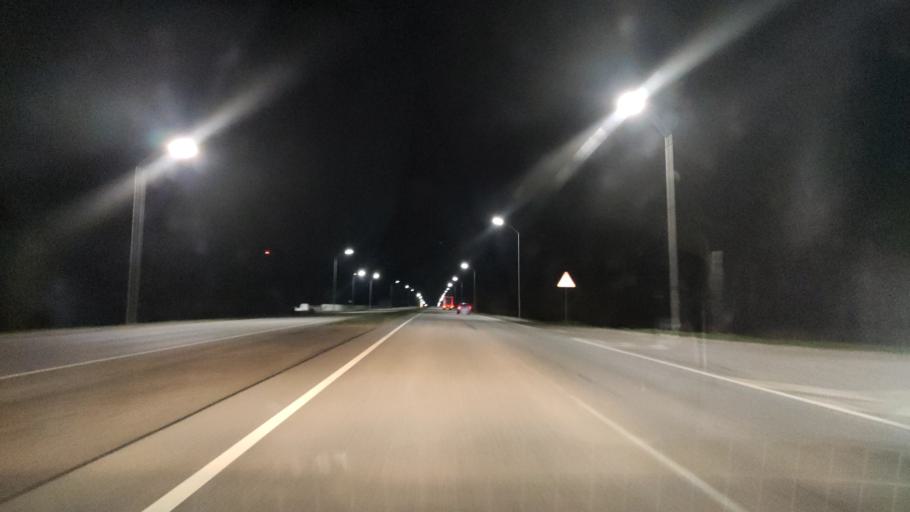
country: RU
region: Belgorod
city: Staryy Oskol
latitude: 51.3656
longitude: 37.8412
